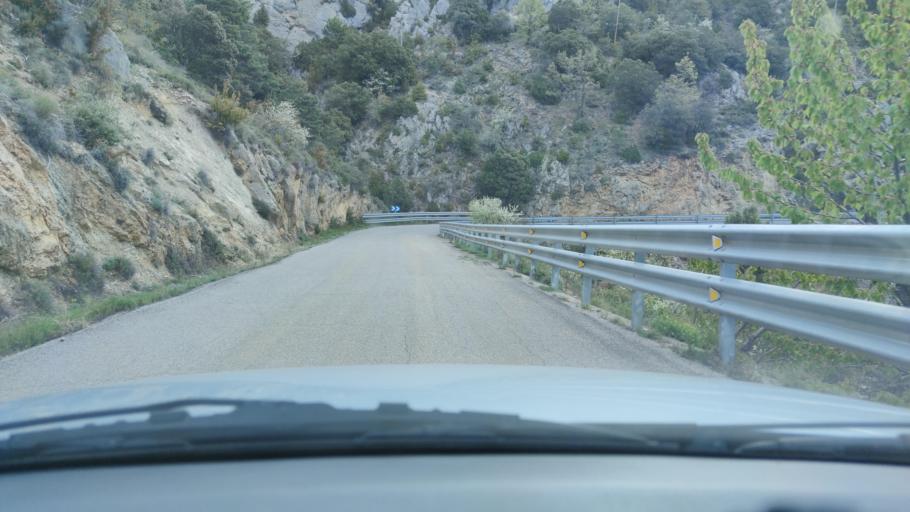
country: ES
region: Catalonia
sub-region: Provincia de Lleida
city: Coll de Nargo
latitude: 42.2443
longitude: 1.3703
